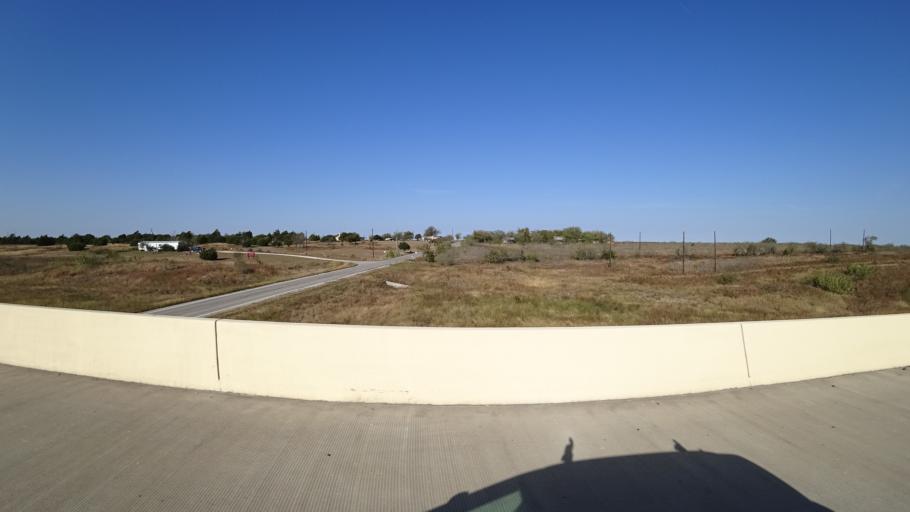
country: US
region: Texas
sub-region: Travis County
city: Onion Creek
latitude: 30.1033
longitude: -97.6689
